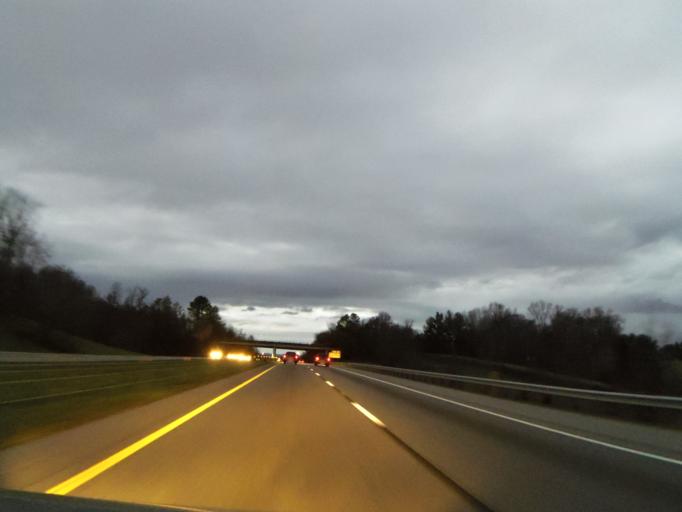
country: US
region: Tennessee
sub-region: Washington County
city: Gray
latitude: 36.3984
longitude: -82.4619
